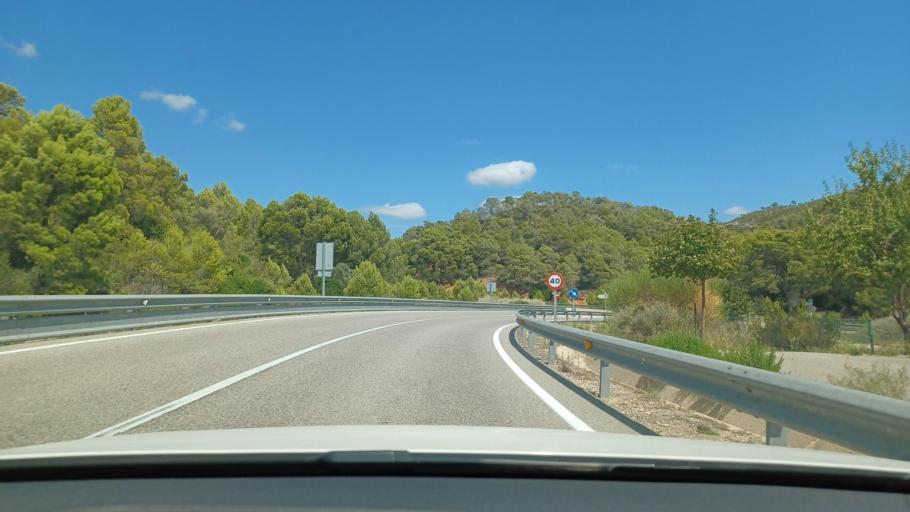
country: ES
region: Catalonia
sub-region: Provincia de Tarragona
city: Bot
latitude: 40.9733
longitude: 0.4443
